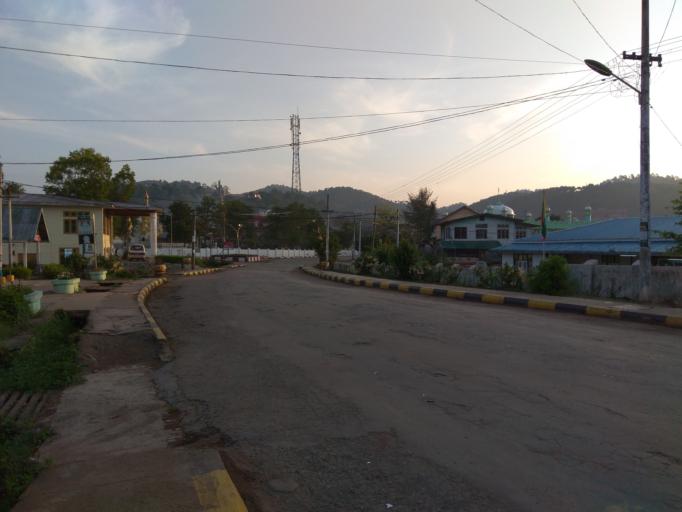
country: MM
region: Mandalay
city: Yamethin
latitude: 20.6326
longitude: 96.5660
